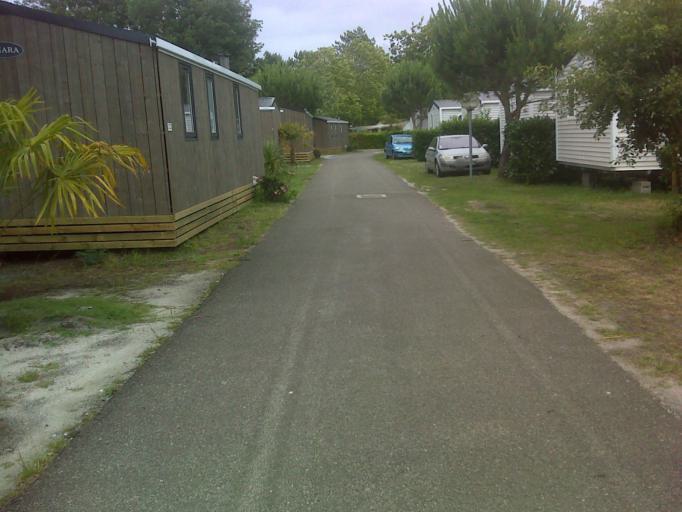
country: FR
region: Aquitaine
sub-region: Departement des Landes
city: Biscarrosse
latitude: 44.4367
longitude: -1.1563
